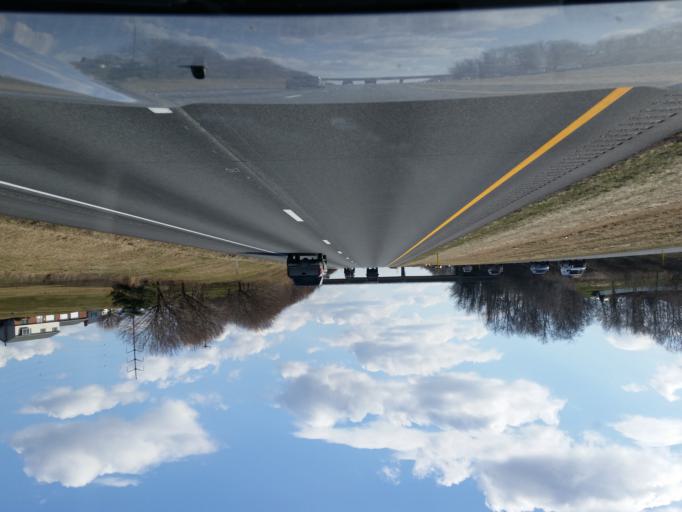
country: US
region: Pennsylvania
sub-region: Lancaster County
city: Rheems
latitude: 40.1536
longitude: -76.5689
